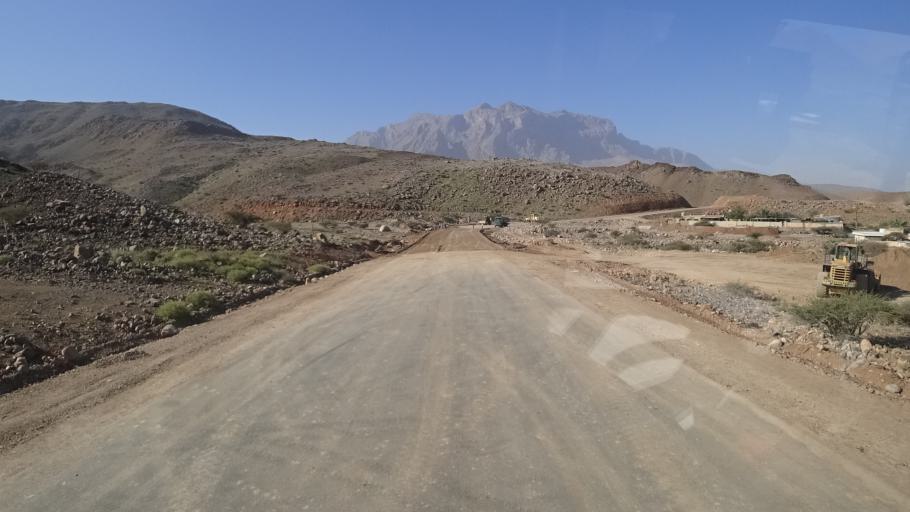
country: OM
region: Muhafazat ad Dakhiliyah
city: Bahla'
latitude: 23.2276
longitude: 57.0693
